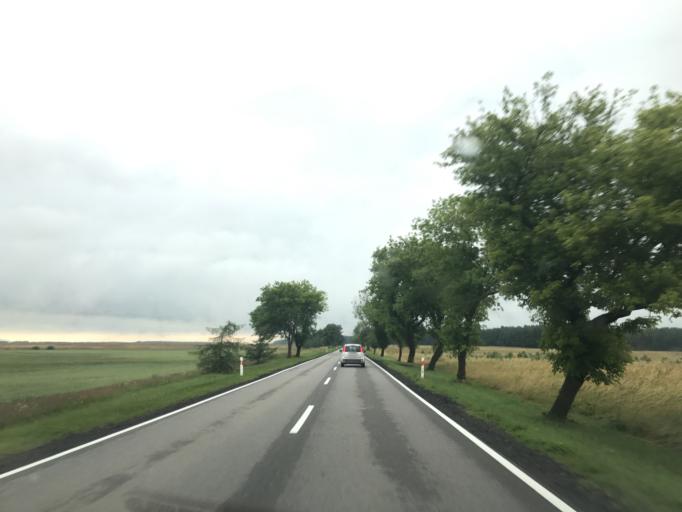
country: PL
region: West Pomeranian Voivodeship
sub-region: Powiat szczecinecki
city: Bialy Bor
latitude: 53.8411
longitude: 16.9103
